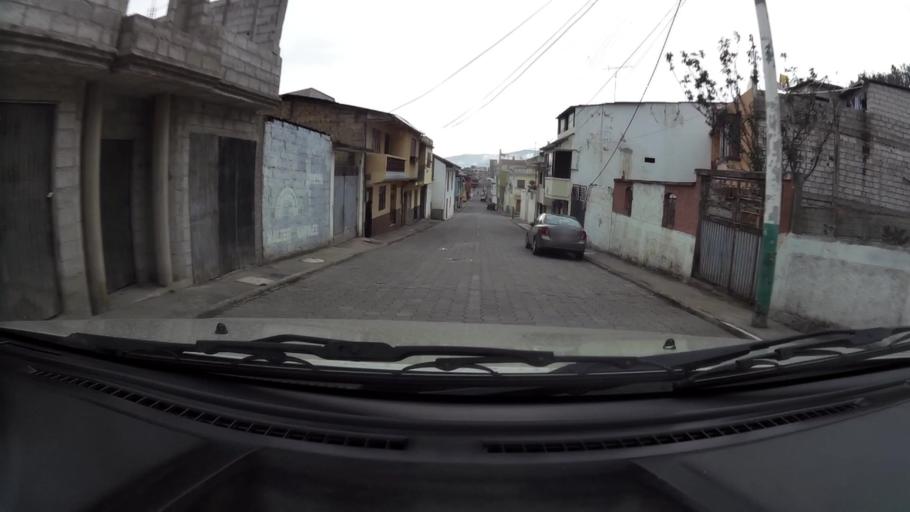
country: EC
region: Chimborazo
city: Alausi
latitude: -2.2900
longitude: -78.9174
